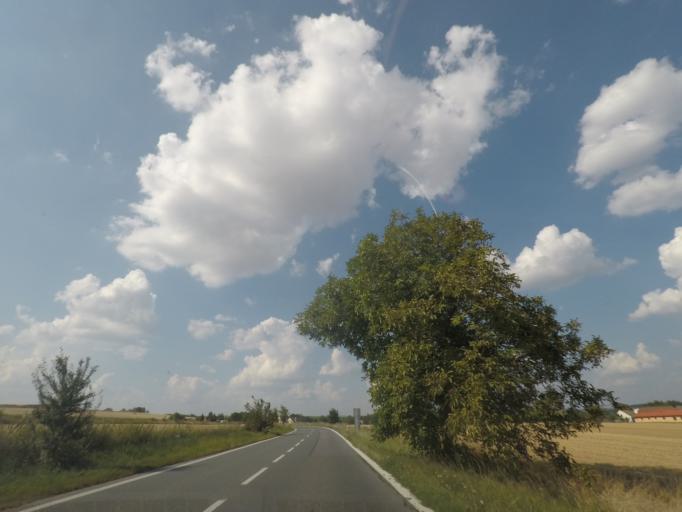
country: CZ
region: Kralovehradecky
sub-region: Okres Nachod
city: Jaromer
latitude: 50.3670
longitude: 15.9069
